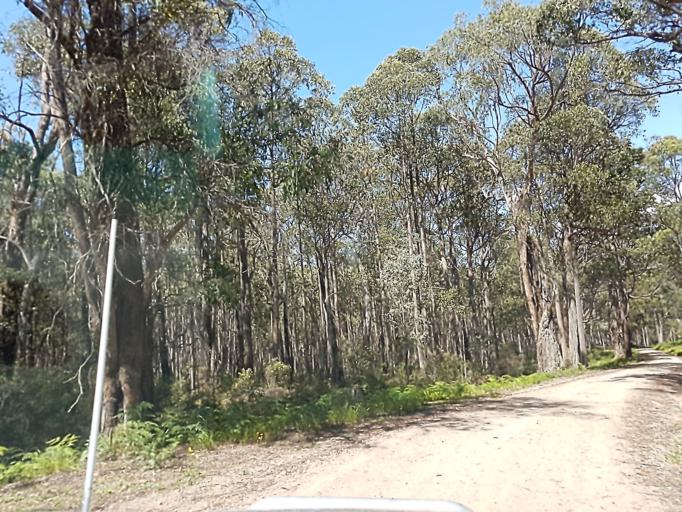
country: AU
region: Victoria
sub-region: East Gippsland
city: Lakes Entrance
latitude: -37.3001
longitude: 148.3277
